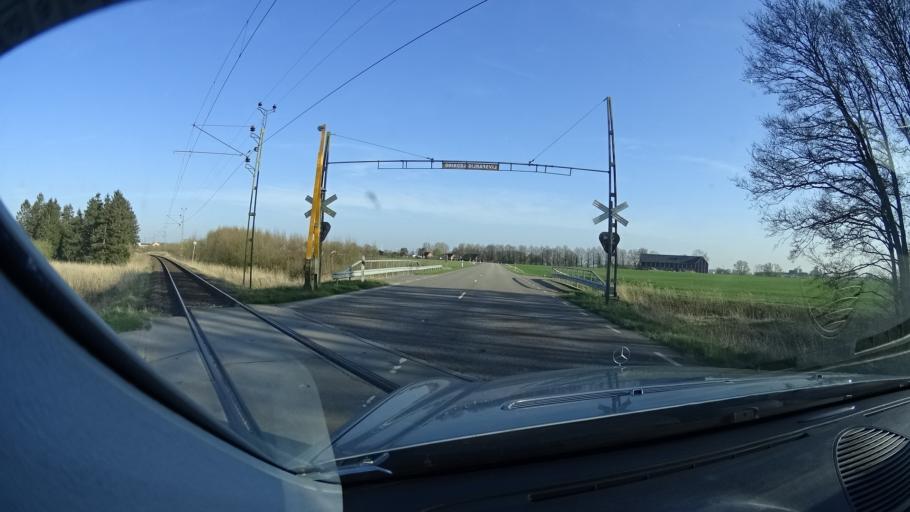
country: SE
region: Skane
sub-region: Svalovs Kommun
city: Svaloev
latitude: 55.8669
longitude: 13.1403
